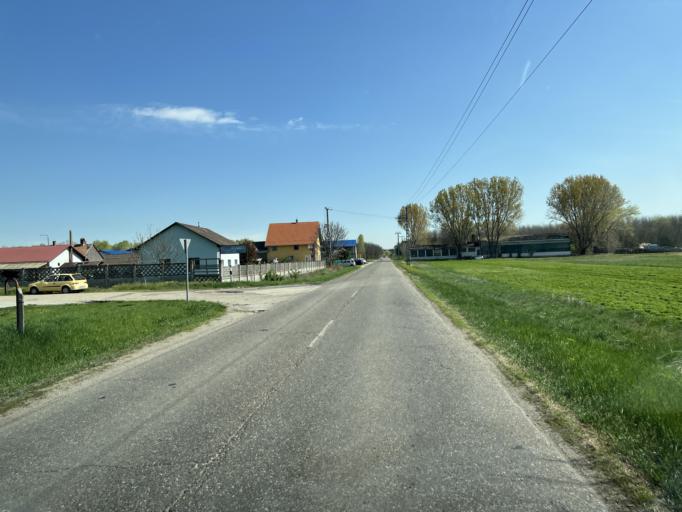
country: HU
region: Pest
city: Felsopakony
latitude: 47.3514
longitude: 19.2533
